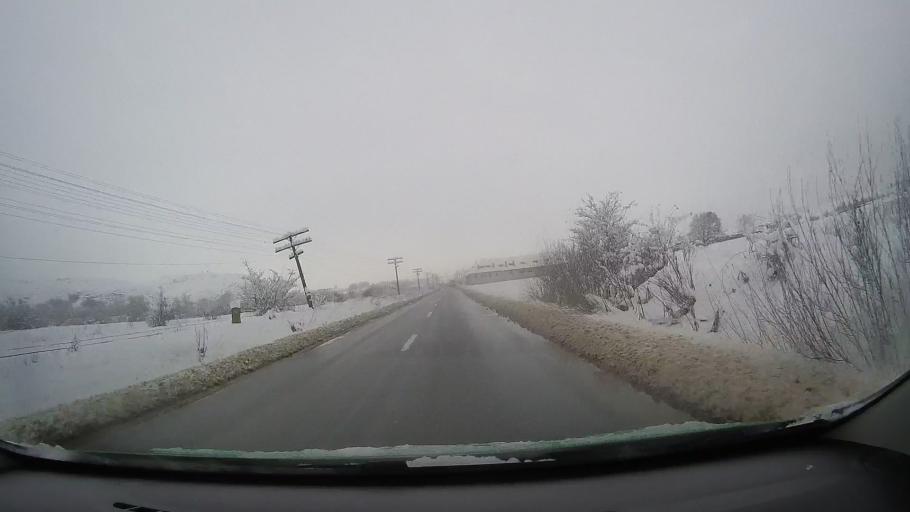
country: RO
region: Sibiu
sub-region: Comuna Orlat
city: Orlat
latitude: 45.7566
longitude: 23.9514
